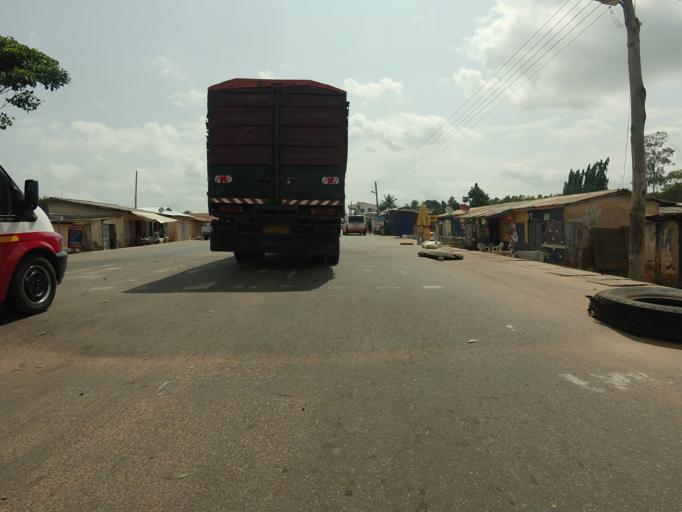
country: TG
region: Maritime
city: Lome
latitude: 6.2316
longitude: 1.0044
